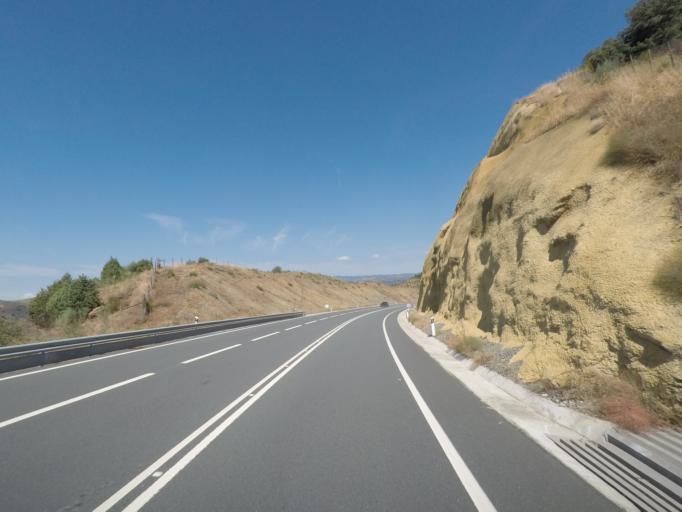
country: PT
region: Braganca
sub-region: Alfandega da Fe
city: Alfandega da Fe
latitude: 41.2976
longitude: -6.8994
